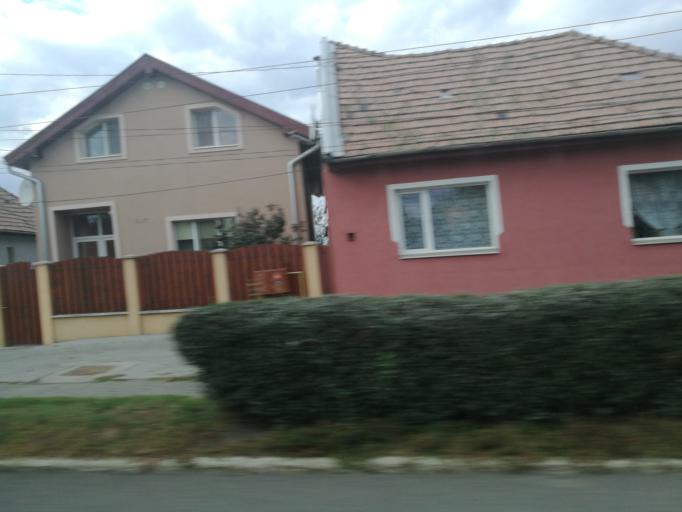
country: RO
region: Mures
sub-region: Comuna Cristesti
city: Cristesti
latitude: 46.5012
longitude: 24.4895
